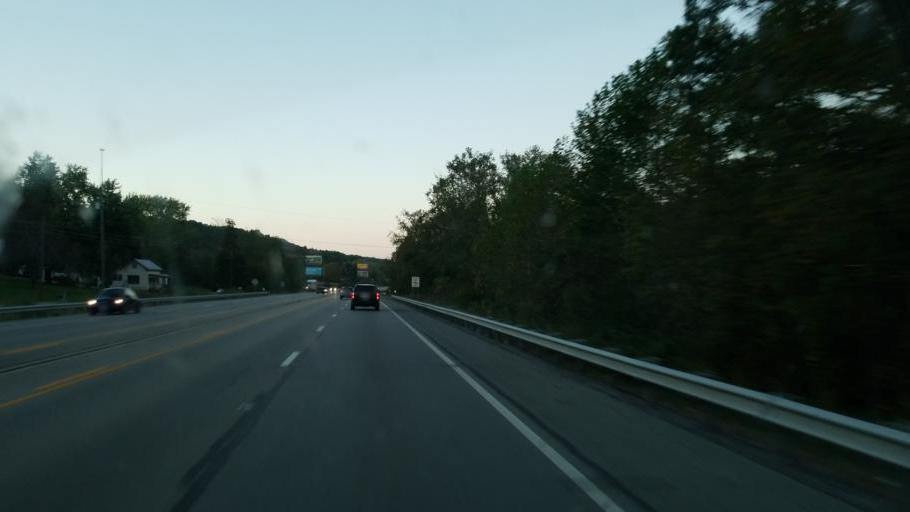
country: US
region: Ohio
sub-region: Ross County
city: Chillicothe
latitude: 39.2327
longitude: -82.9844
